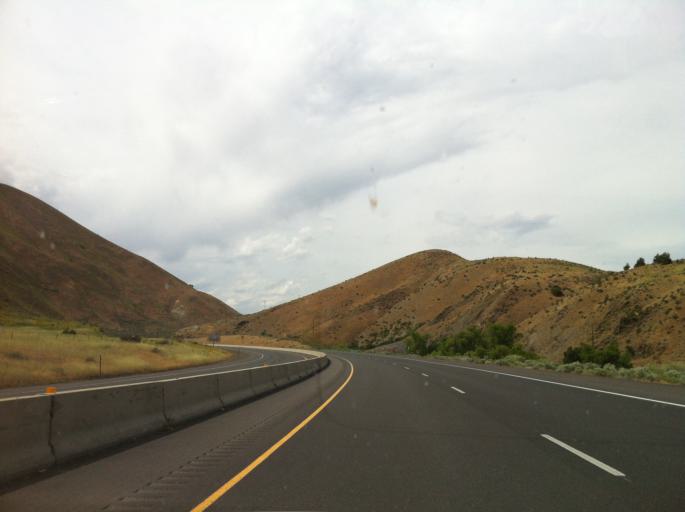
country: US
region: Idaho
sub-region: Washington County
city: Weiser
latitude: 44.4037
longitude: -117.3109
